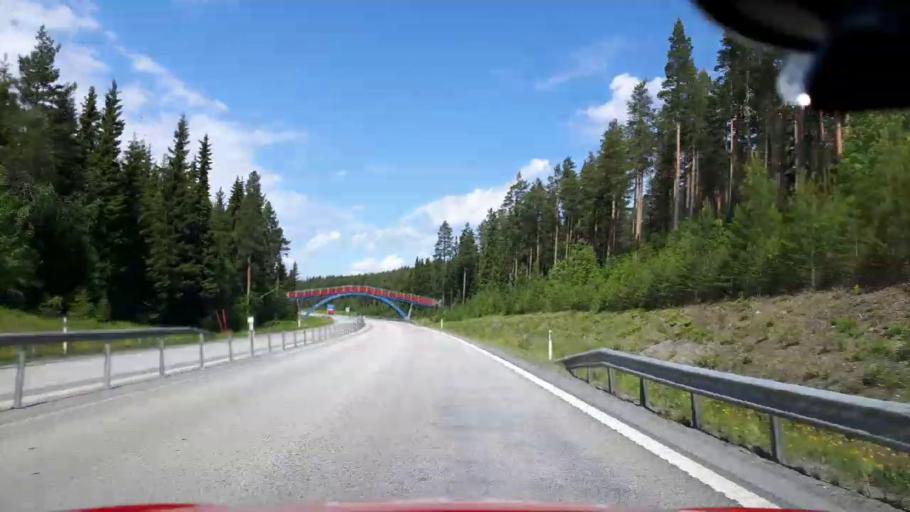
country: SE
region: Jaemtland
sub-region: OEstersunds Kommun
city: Ostersund
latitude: 63.1918
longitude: 14.6901
